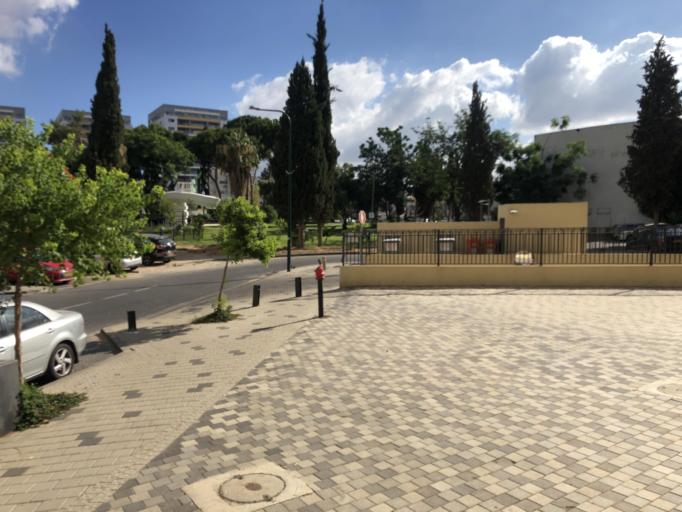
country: IL
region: Central District
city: Yehud
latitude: 32.0300
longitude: 34.8875
